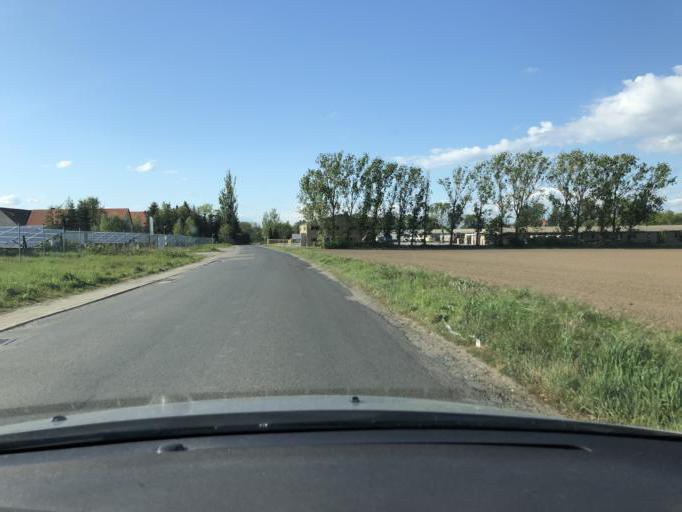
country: DE
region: Thuringia
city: Gerstenberg
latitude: 51.0128
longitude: 12.4386
